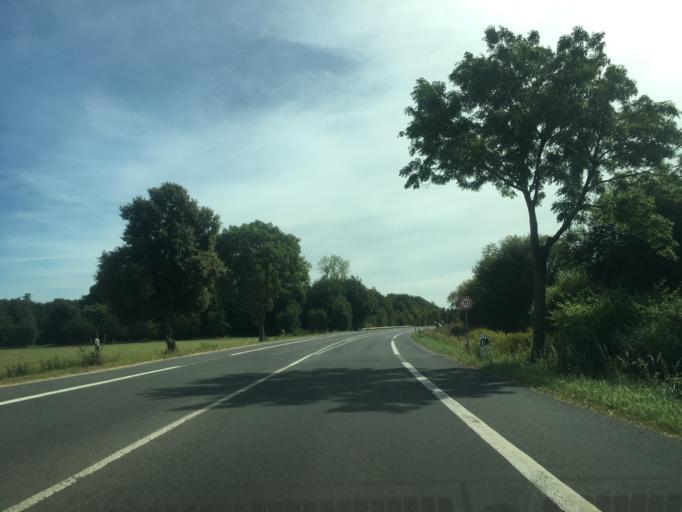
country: DE
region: North Rhine-Westphalia
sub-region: Regierungsbezirk Koln
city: Titz
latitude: 51.0523
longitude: 6.3873
